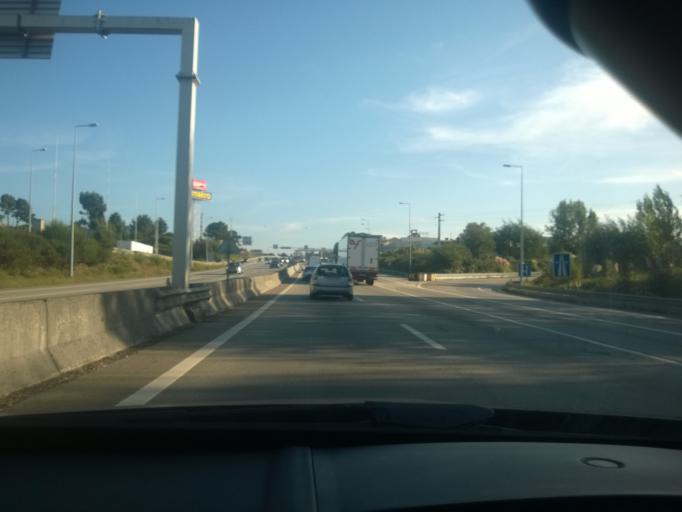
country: PT
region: Porto
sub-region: Maia
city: Leca do Bailio
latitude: 41.2021
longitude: -8.6275
